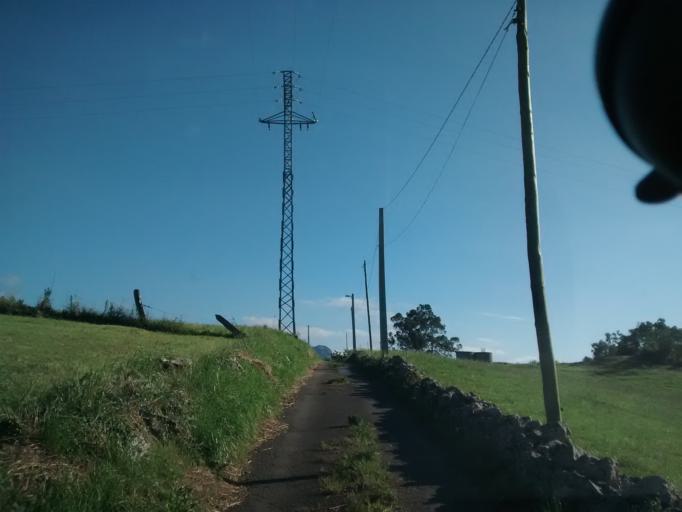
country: ES
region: Cantabria
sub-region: Provincia de Cantabria
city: Entrambasaguas
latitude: 43.3637
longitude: -3.7072
